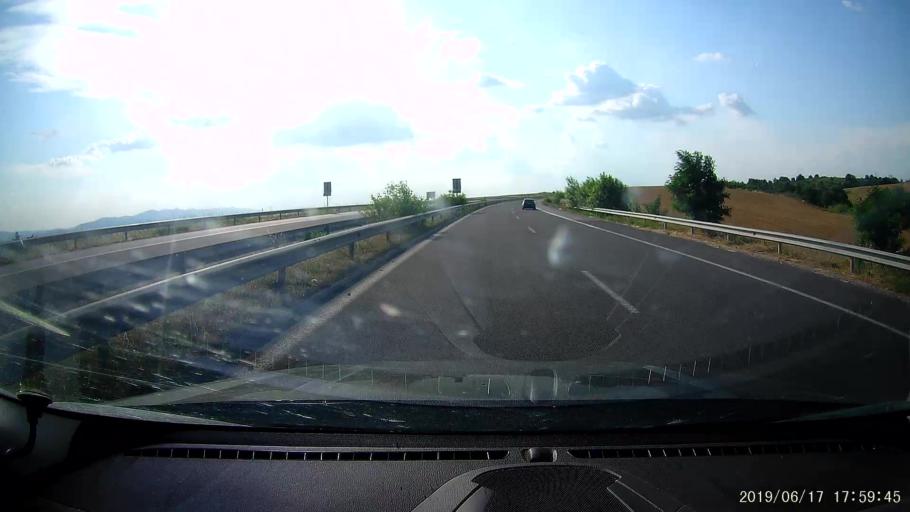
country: BG
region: Khaskovo
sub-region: Obshtina Svilengrad
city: Svilengrad
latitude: 41.7263
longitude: 26.2904
